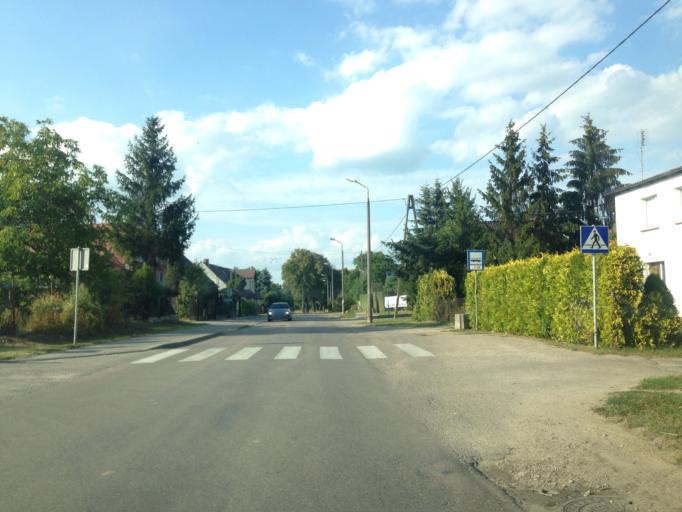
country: PL
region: Warmian-Masurian Voivodeship
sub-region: Powiat ilawski
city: Ilawa
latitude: 53.6166
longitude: 19.5678
